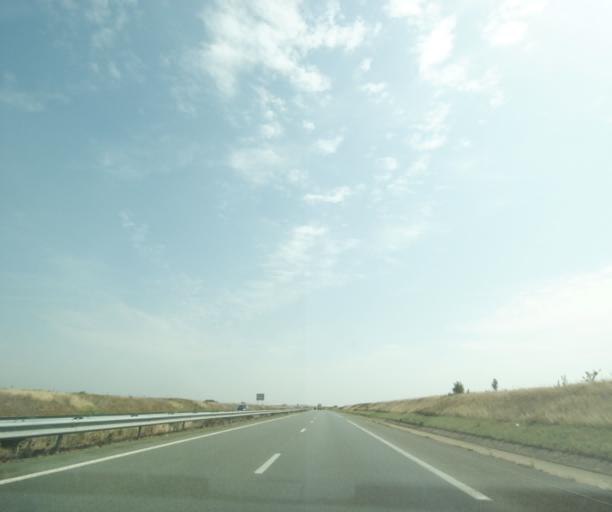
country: FR
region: Pays de la Loire
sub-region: Departement de la Vendee
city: Le Langon
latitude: 46.4625
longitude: -0.9003
